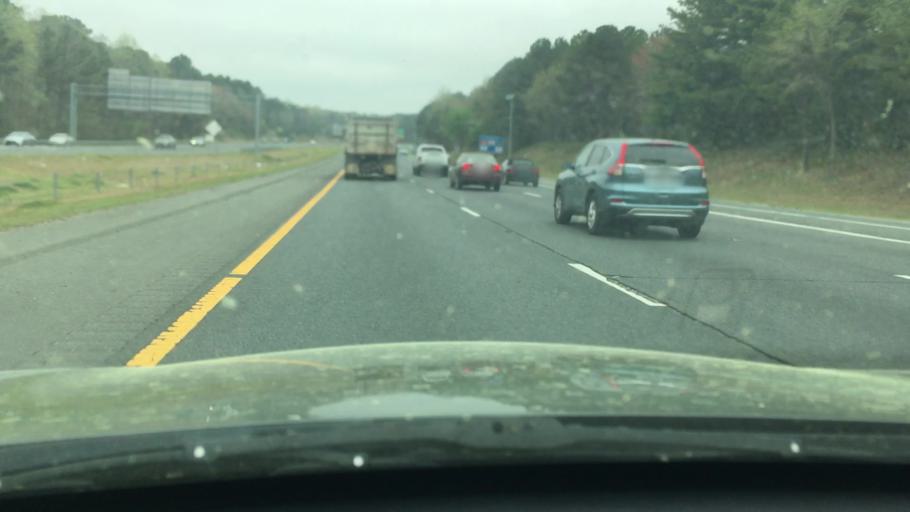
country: US
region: North Carolina
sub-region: Wake County
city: Cary
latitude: 35.7717
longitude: -78.7402
